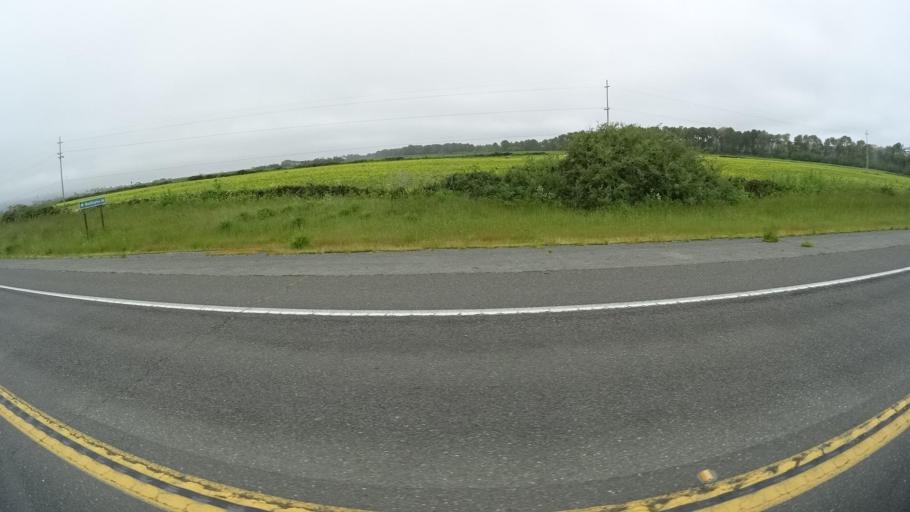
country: US
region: California
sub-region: Humboldt County
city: Fortuna
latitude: 40.6073
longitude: -124.2065
